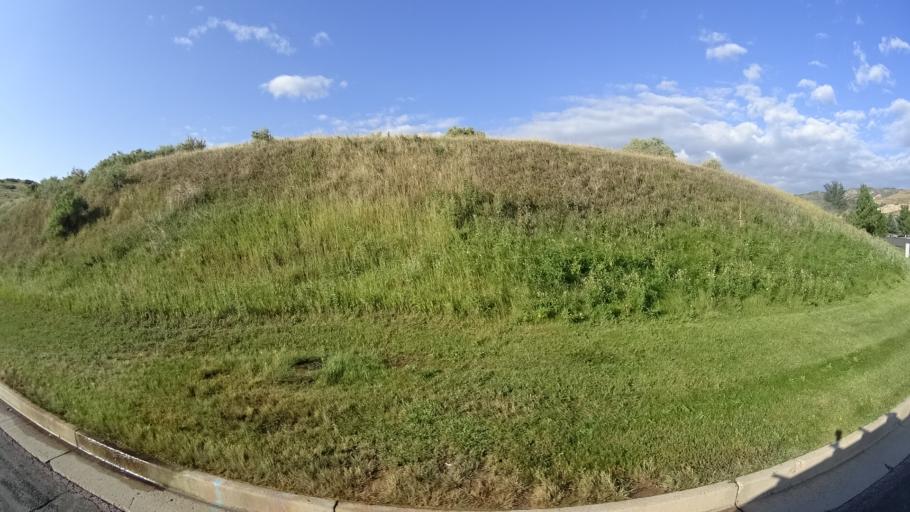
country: US
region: Colorado
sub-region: El Paso County
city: Manitou Springs
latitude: 38.8954
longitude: -104.8679
